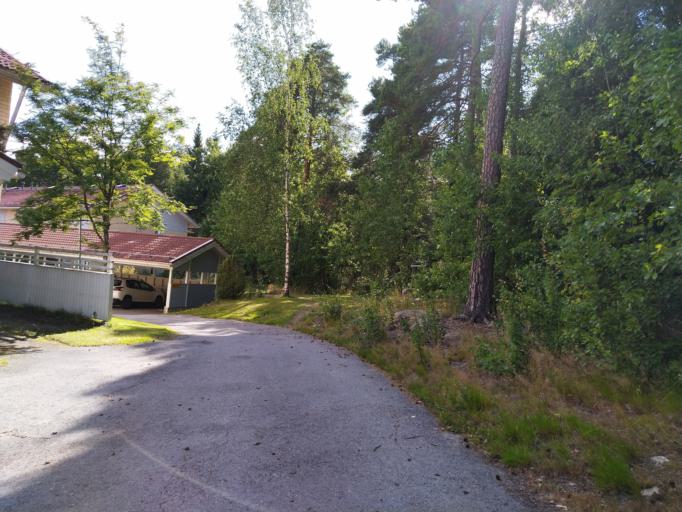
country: FI
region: Varsinais-Suomi
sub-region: Turku
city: Kaarina
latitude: 60.4468
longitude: 22.3349
